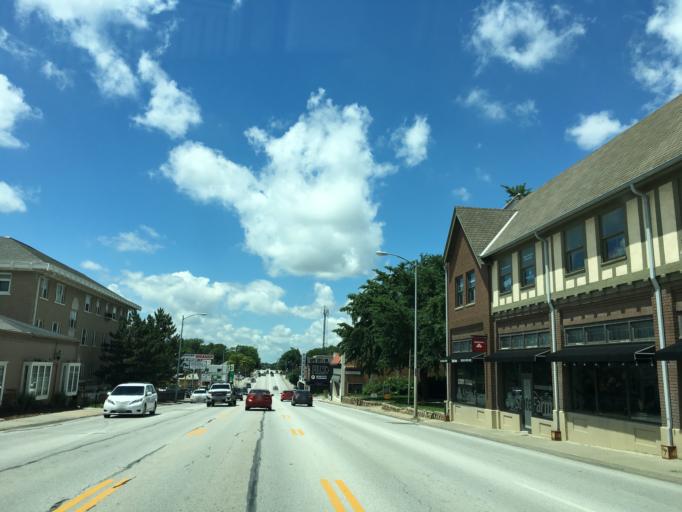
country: US
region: Nebraska
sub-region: Douglas County
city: Omaha
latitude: 41.2596
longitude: -95.9879
